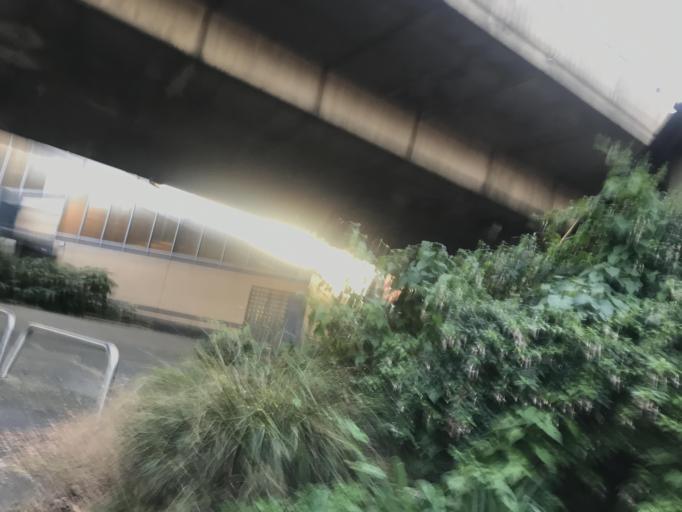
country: GB
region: England
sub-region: Greater London
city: Hammersmith
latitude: 51.5160
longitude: -0.2200
